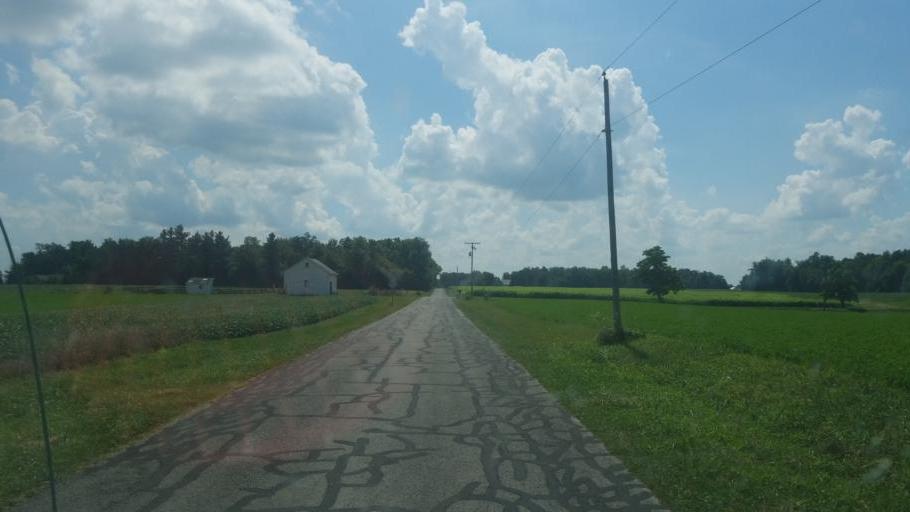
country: US
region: Ohio
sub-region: Hancock County
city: Arlington
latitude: 40.8906
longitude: -83.7080
